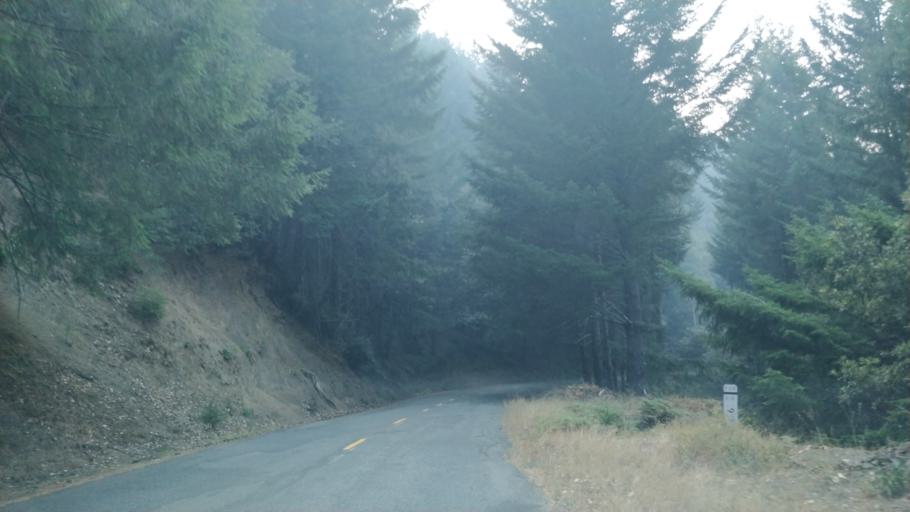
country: US
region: California
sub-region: Humboldt County
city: Rio Dell
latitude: 40.3020
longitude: -124.0585
